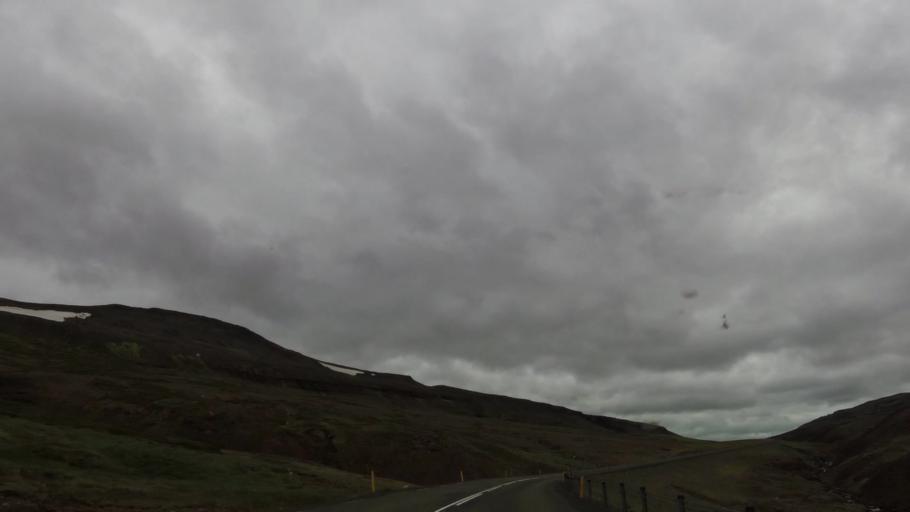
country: IS
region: West
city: Borgarnes
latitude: 65.3374
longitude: -21.7470
